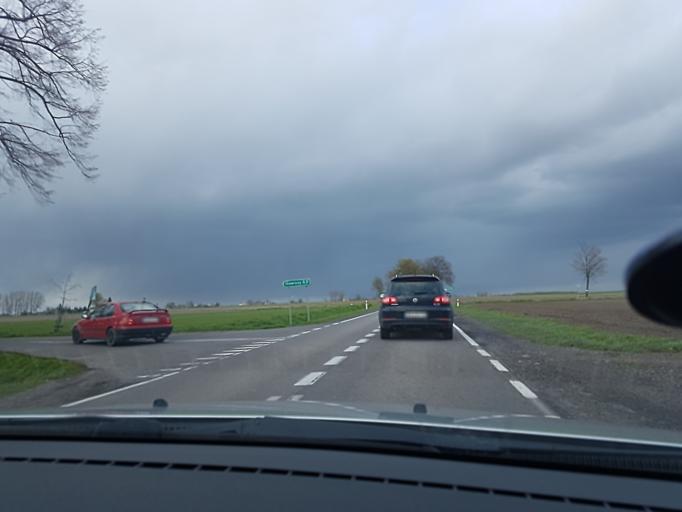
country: PL
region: Lodz Voivodeship
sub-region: Powiat leczycki
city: Leczyca
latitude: 52.1083
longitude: 19.2401
